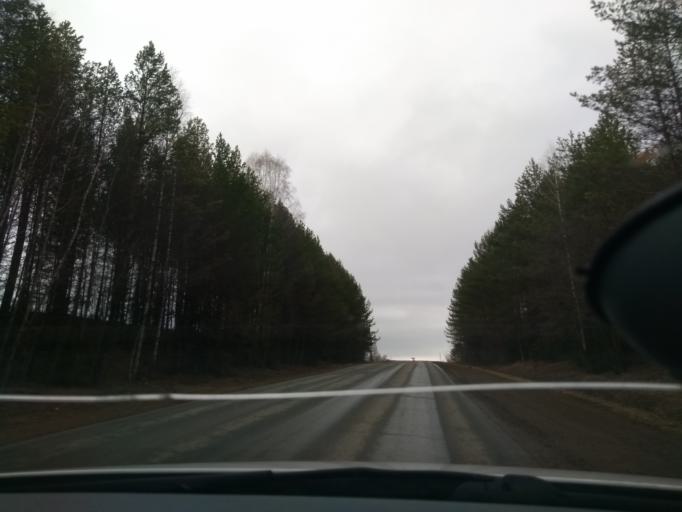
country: RU
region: Perm
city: Kungur
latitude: 57.3723
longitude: 56.8363
